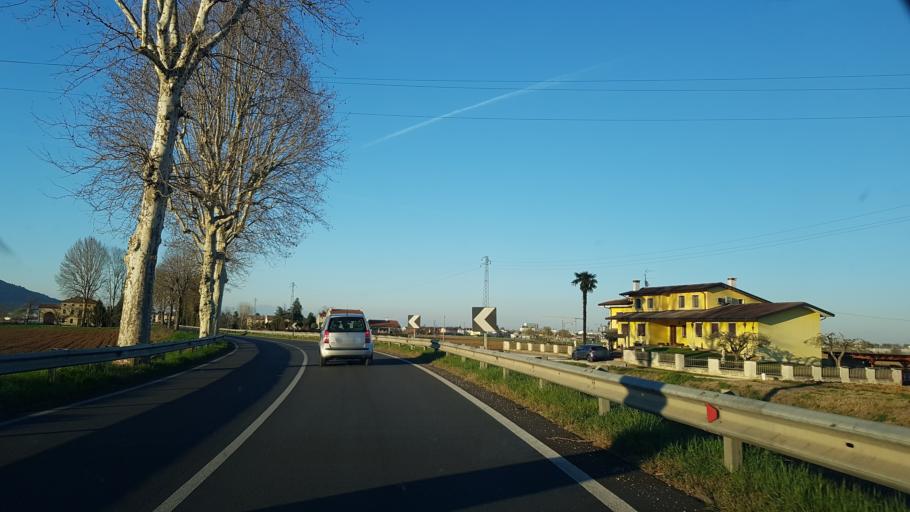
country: IT
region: Veneto
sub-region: Provincia di Vicenza
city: Ponte di Nanto
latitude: 45.4295
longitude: 11.5976
